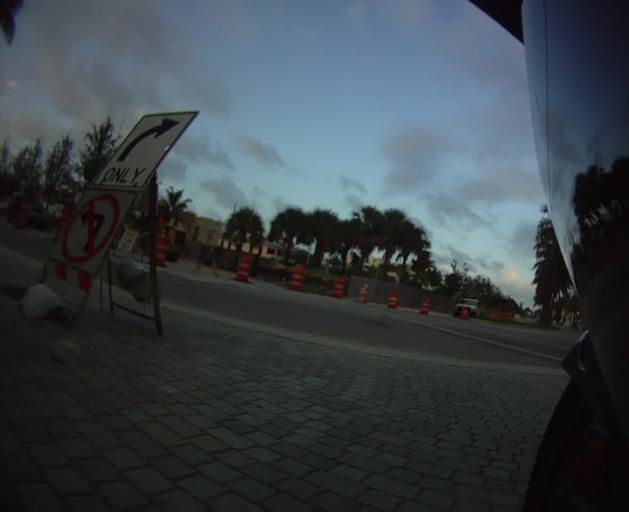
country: US
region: Florida
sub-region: Miami-Dade County
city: Miami Beach
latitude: 25.7682
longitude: -80.1371
